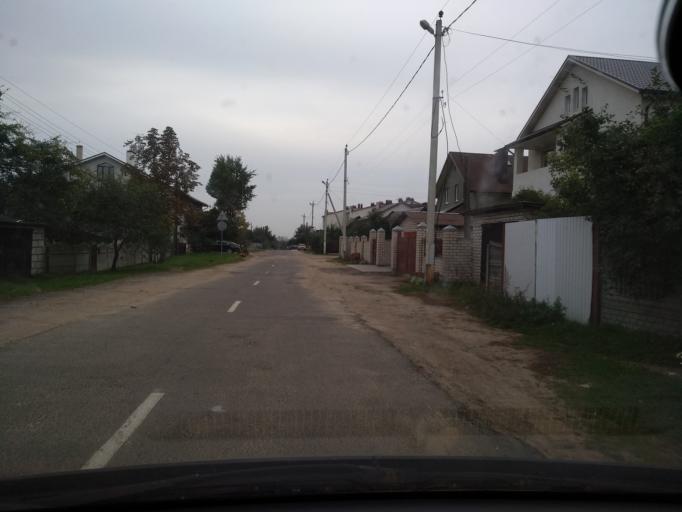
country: BY
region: Minsk
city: Minsk
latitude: 53.9434
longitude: 27.5851
